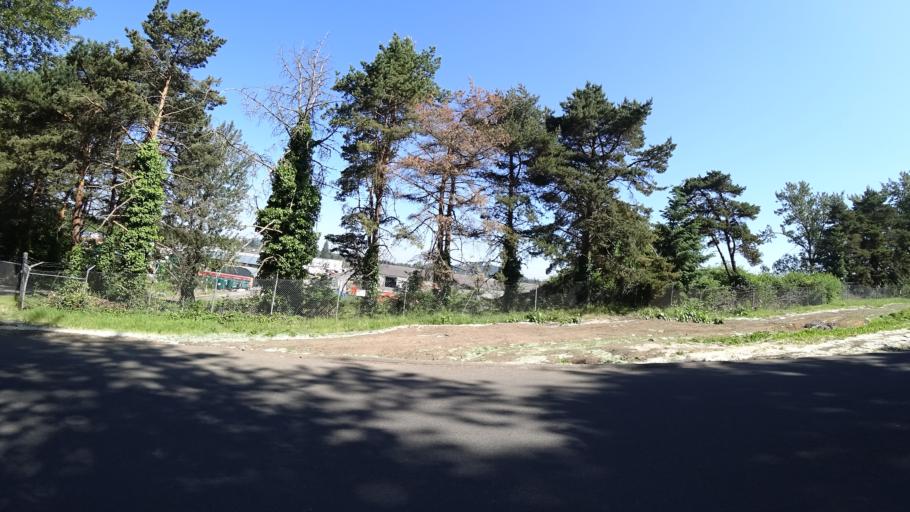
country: US
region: Oregon
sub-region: Multnomah County
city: Lents
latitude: 45.4697
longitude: -122.5596
